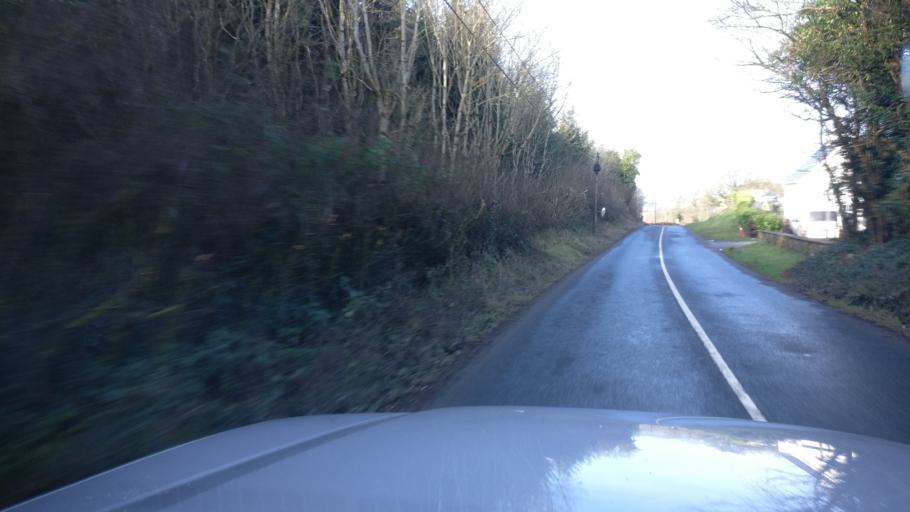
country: IE
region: Leinster
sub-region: Laois
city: Stradbally
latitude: 52.9438
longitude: -7.2002
